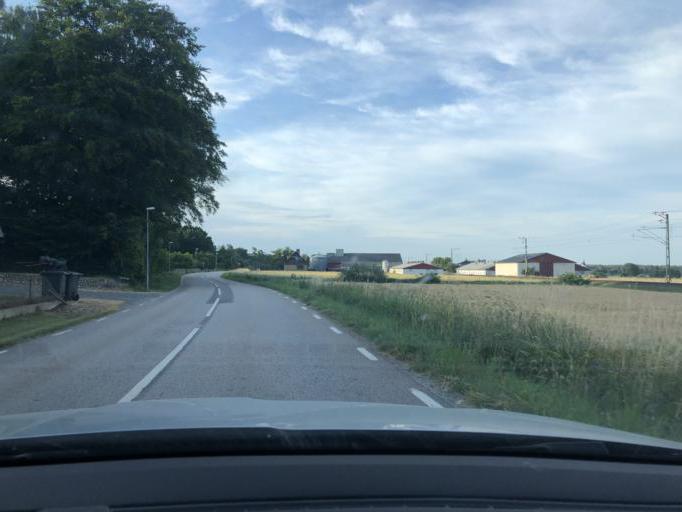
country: SE
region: Blekinge
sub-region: Solvesborgs Kommun
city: Soelvesborg
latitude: 56.0984
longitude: 14.6168
